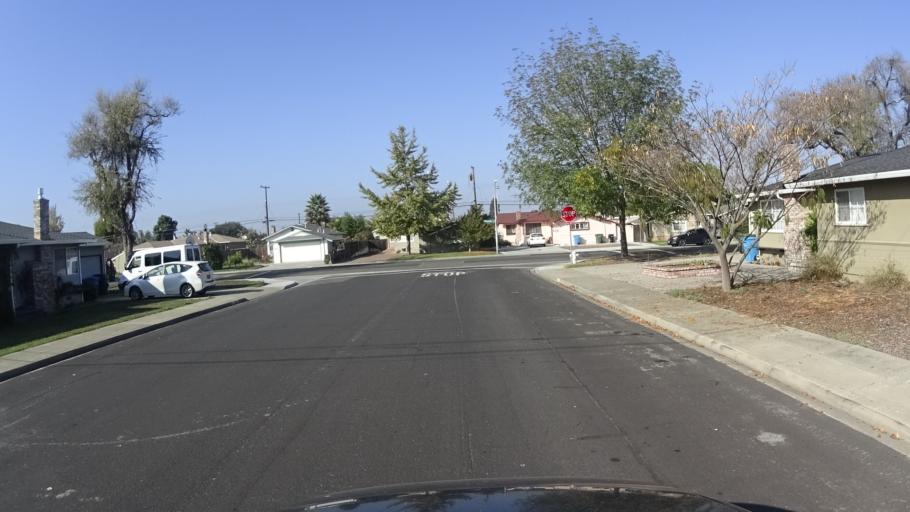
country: US
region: California
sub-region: Santa Clara County
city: Santa Clara
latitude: 37.3629
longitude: -121.9828
